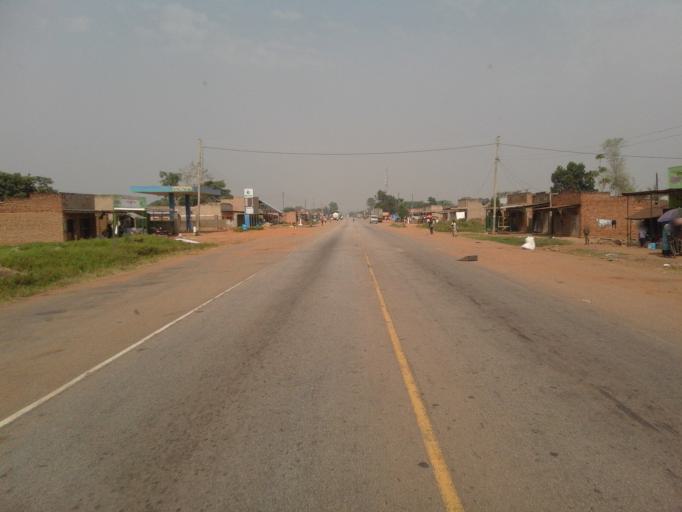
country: UG
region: Eastern Region
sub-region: Bugiri District
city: Bugiri
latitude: 0.6027
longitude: 33.6954
